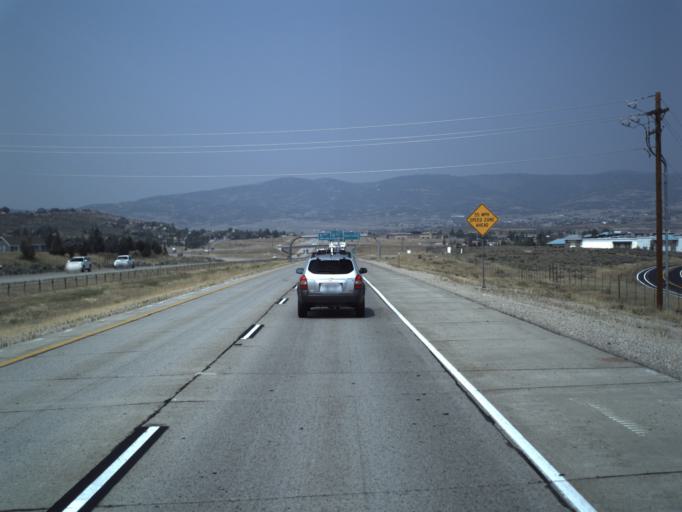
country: US
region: Utah
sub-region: Summit County
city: Snyderville
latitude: 40.7114
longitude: -111.4818
